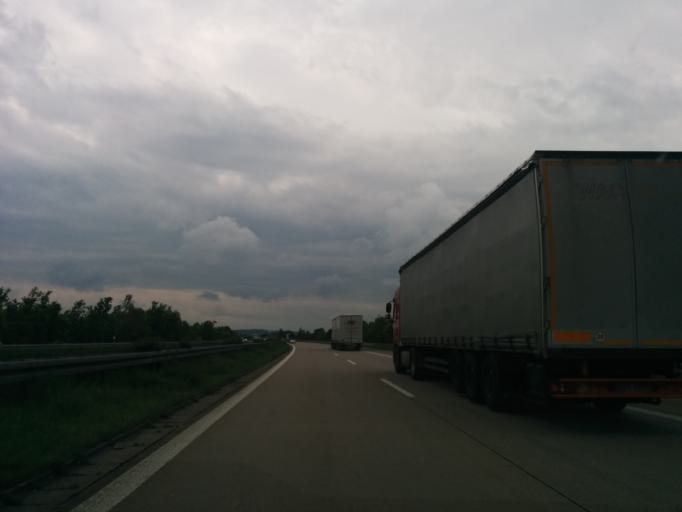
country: DE
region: Bavaria
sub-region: Regierungsbezirk Mittelfranken
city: Schopfloch
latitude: 49.1618
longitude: 10.2619
